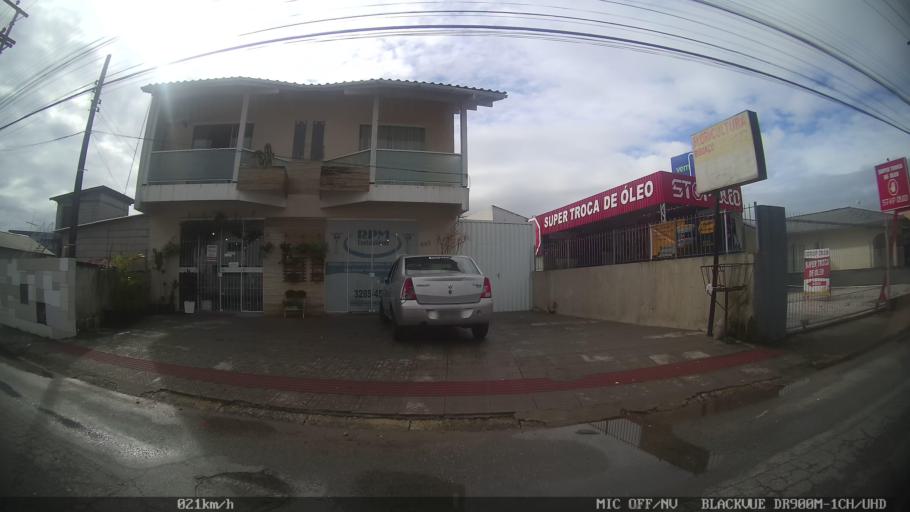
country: BR
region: Santa Catarina
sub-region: Biguacu
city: Biguacu
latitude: -27.5023
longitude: -48.6539
